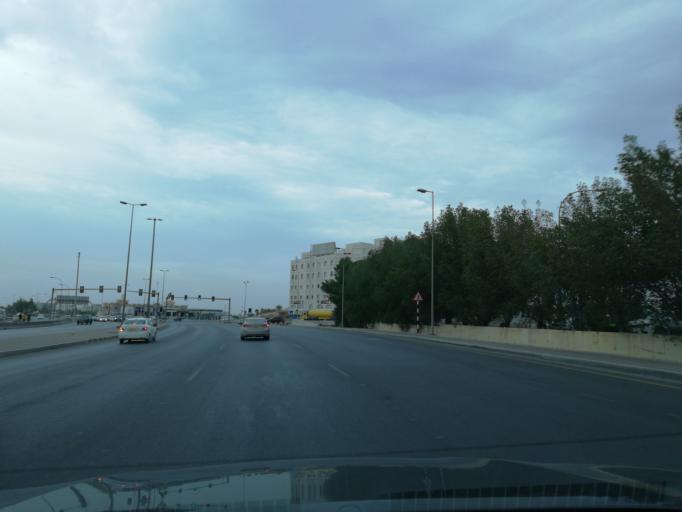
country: OM
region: Muhafazat Masqat
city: Bawshar
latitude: 23.5739
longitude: 58.3825
